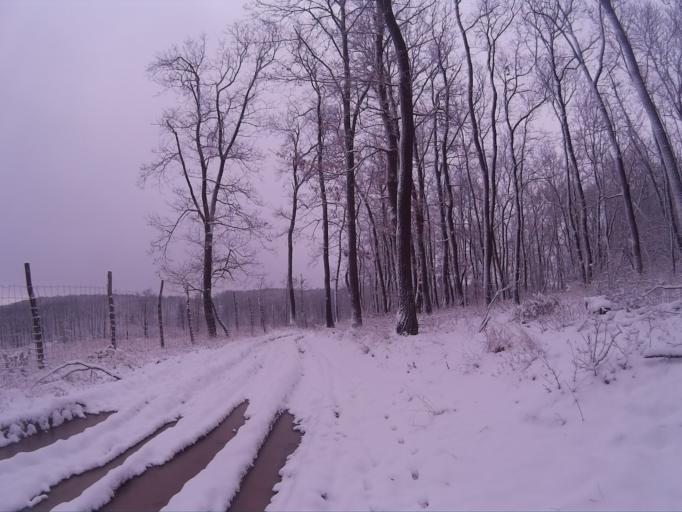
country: HU
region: Komarom-Esztergom
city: Tarjan
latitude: 47.5645
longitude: 18.5338
